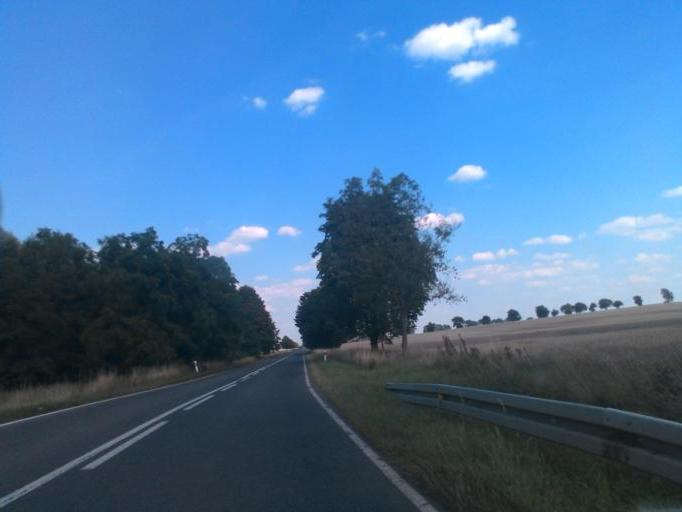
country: PL
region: West Pomeranian Voivodeship
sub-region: Powiat pyrzycki
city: Pyrzyce
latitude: 53.1413
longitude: 14.9811
